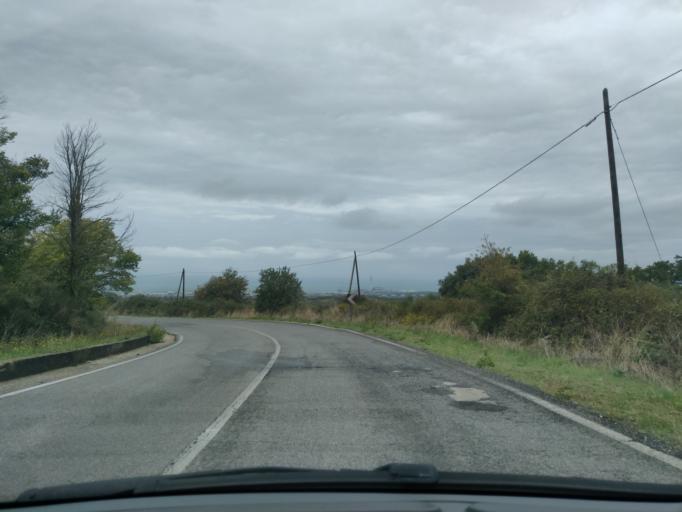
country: IT
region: Latium
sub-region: Citta metropolitana di Roma Capitale
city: Civitavecchia
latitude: 42.1144
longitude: 11.8550
